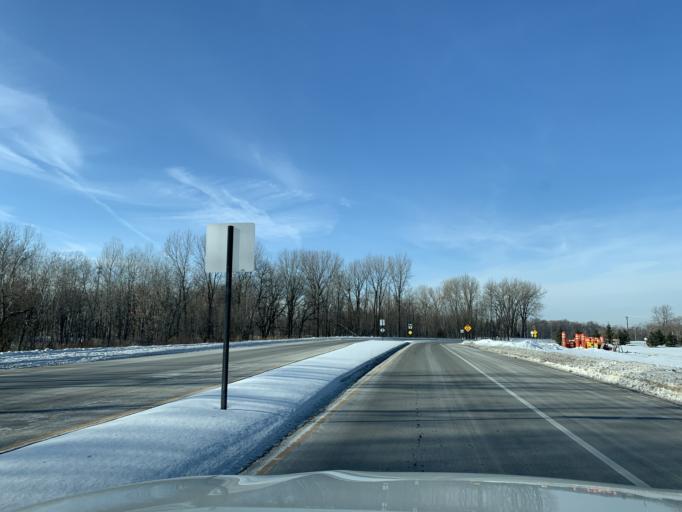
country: US
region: Minnesota
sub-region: Anoka County
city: Columbus
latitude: 45.2483
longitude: -93.0282
